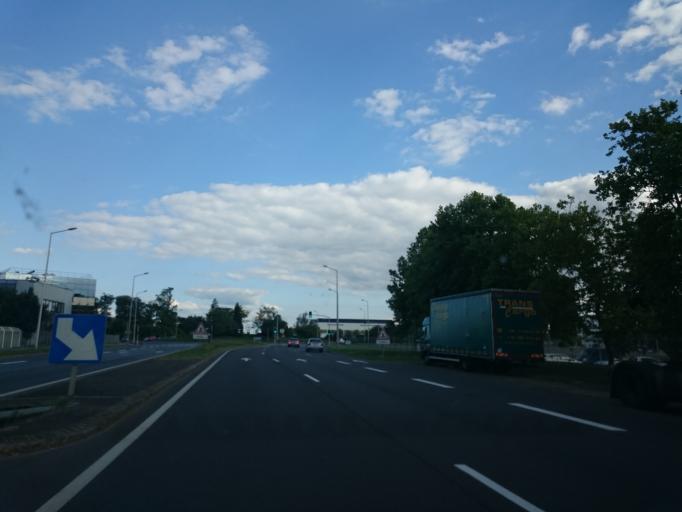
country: FR
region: Ile-de-France
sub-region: Departement de l'Essonne
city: Evry
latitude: 48.6210
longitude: 2.4502
